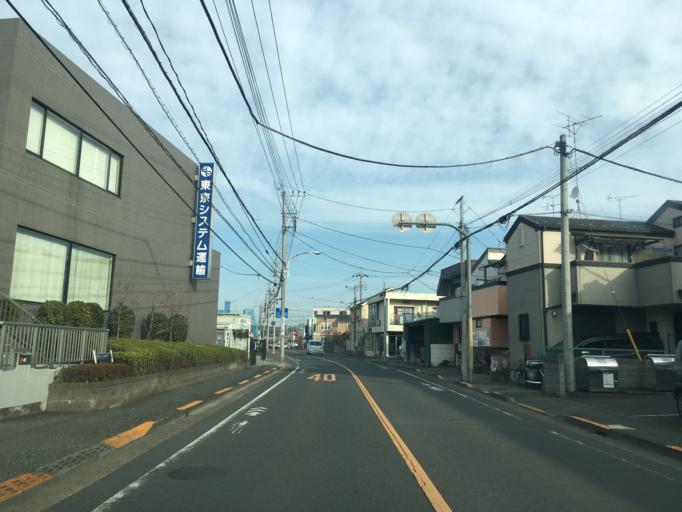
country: JP
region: Tokyo
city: Higashimurayama-shi
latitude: 35.7454
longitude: 139.4287
